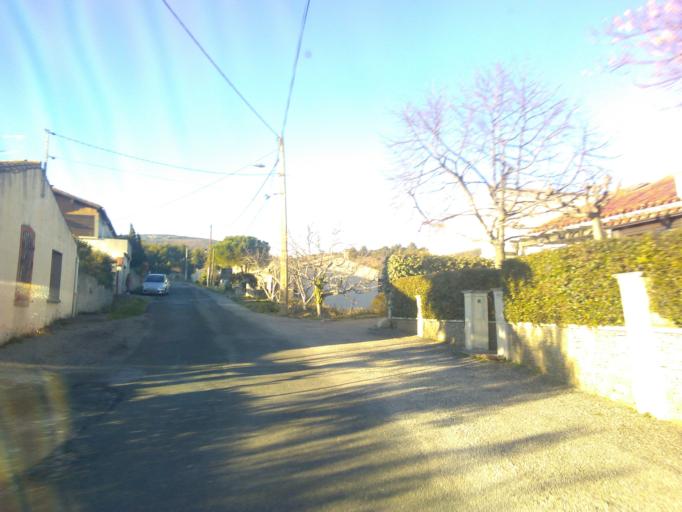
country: FR
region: Languedoc-Roussillon
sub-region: Departement de l'Aude
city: Caunes-Minervois
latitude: 43.3291
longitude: 2.5306
